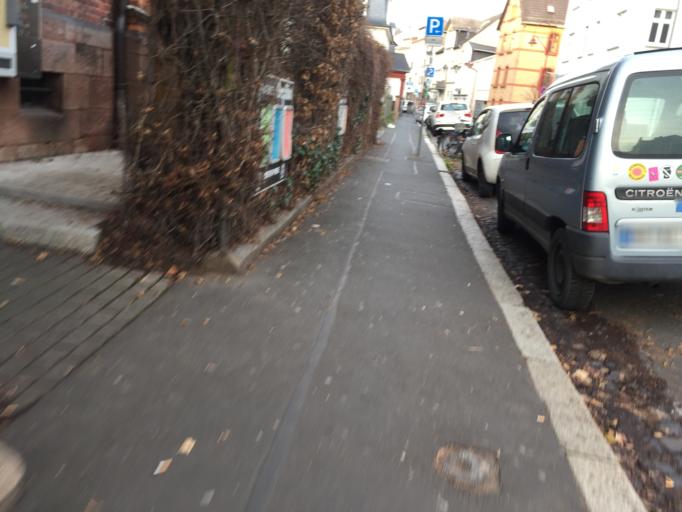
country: DE
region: Hesse
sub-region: Regierungsbezirk Giessen
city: Marburg an der Lahn
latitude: 50.8050
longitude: 8.7710
